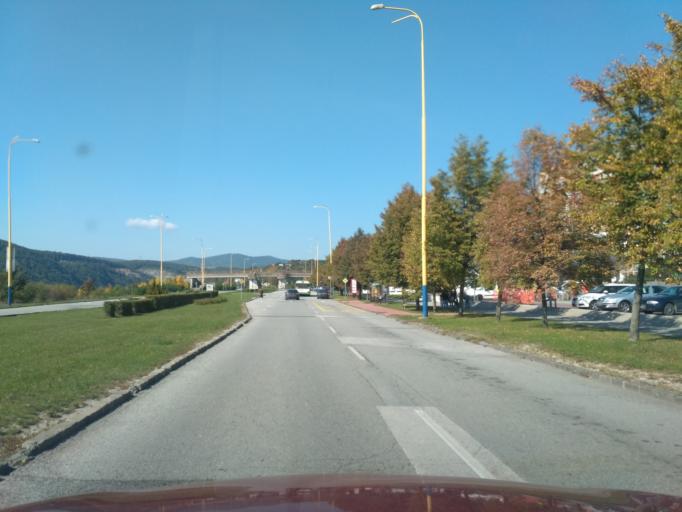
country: SK
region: Kosicky
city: Kosice
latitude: 48.7563
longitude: 21.2648
